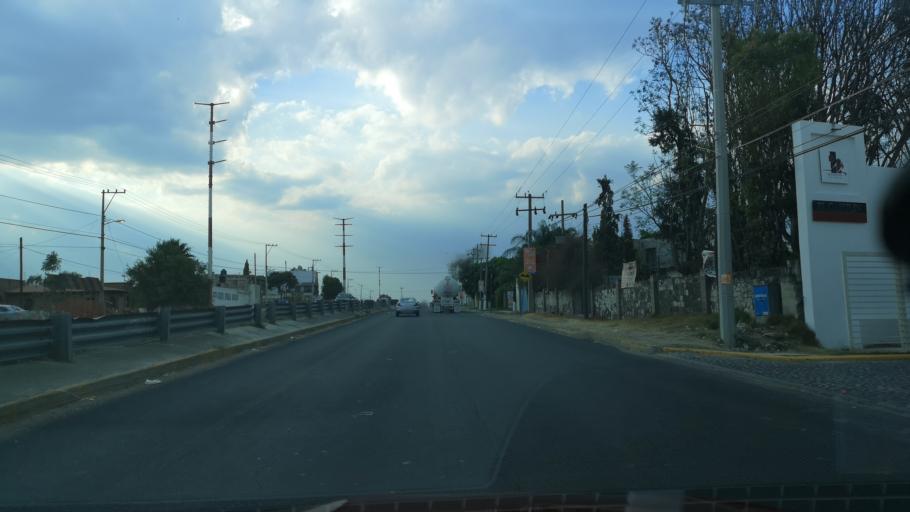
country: MX
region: Puebla
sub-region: Juan C. Bonilla
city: Santa Maria Zacatepec
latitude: 19.1120
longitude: -98.3554
